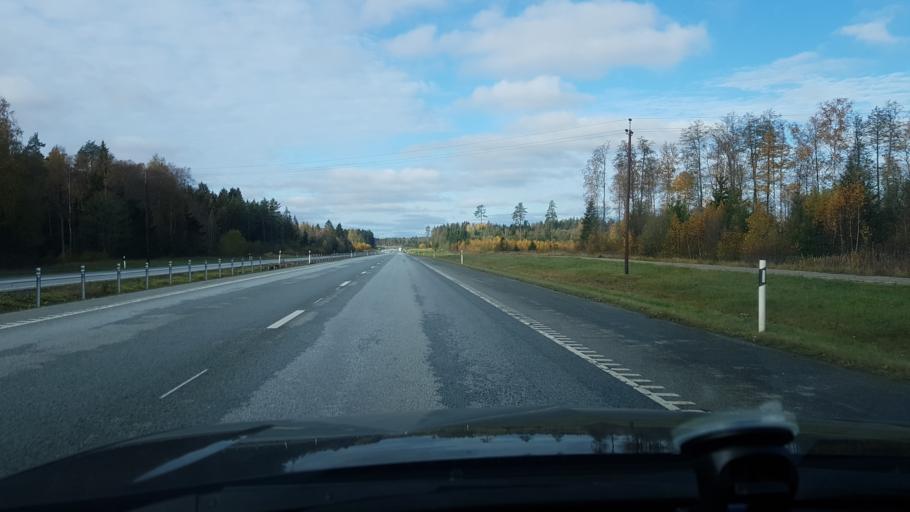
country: EE
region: Laeaene-Virumaa
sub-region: Kadrina vald
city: Kadrina
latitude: 59.4545
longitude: 26.0528
